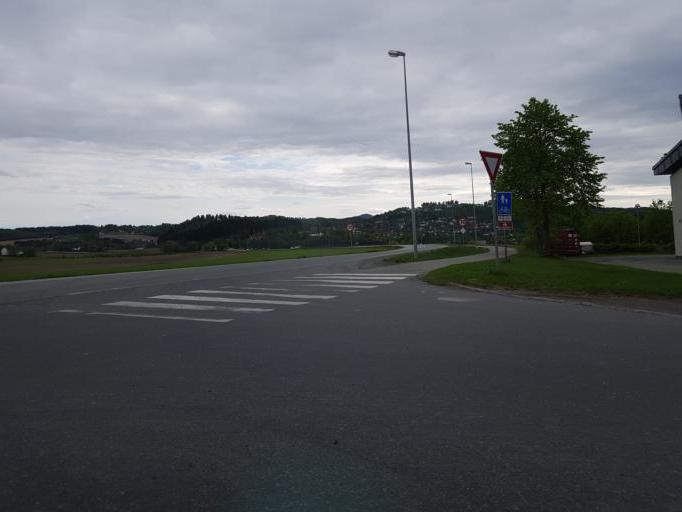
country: NO
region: Nord-Trondelag
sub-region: Levanger
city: Levanger
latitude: 63.7392
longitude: 11.2830
